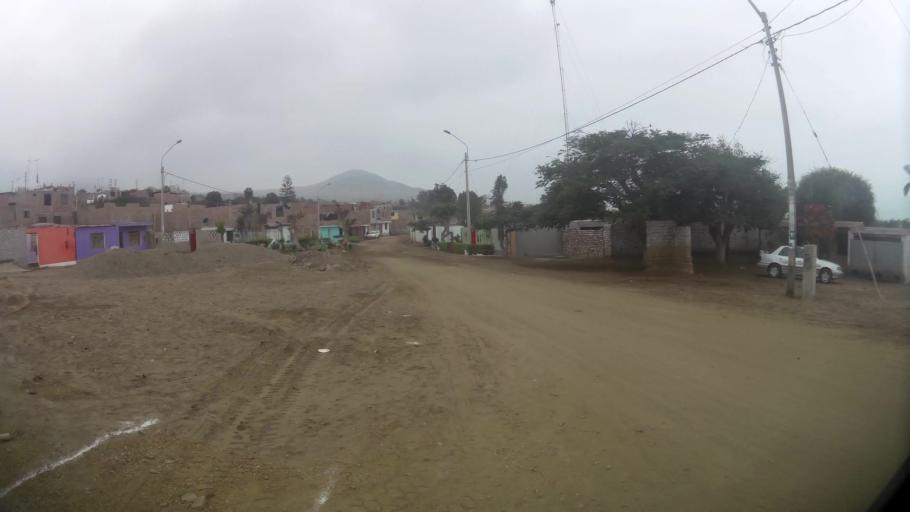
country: PE
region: Lima
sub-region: Provincia de Huaral
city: Chancay
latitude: -11.5910
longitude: -77.2623
